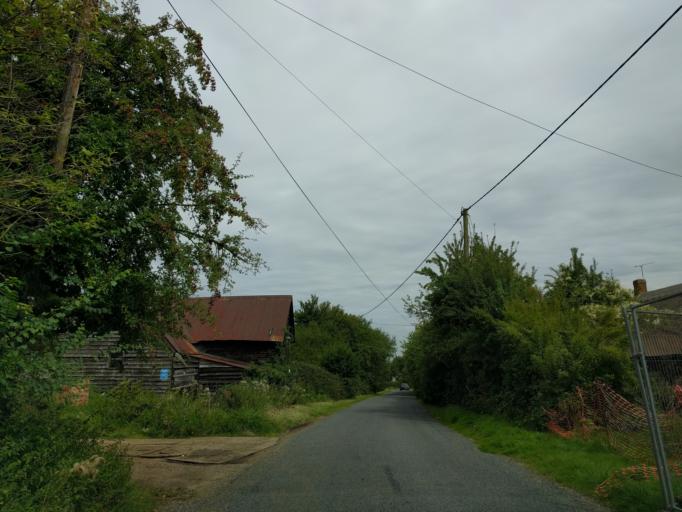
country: GB
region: England
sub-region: Essex
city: Great Dunmow
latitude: 51.8376
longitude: 0.4136
